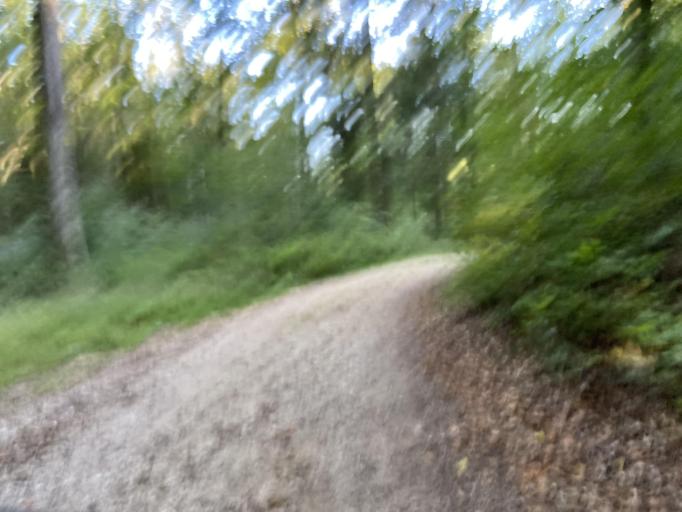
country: DE
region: Baden-Wuerttemberg
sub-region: Tuebingen Region
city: Bingen
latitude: 48.1329
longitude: 9.2746
